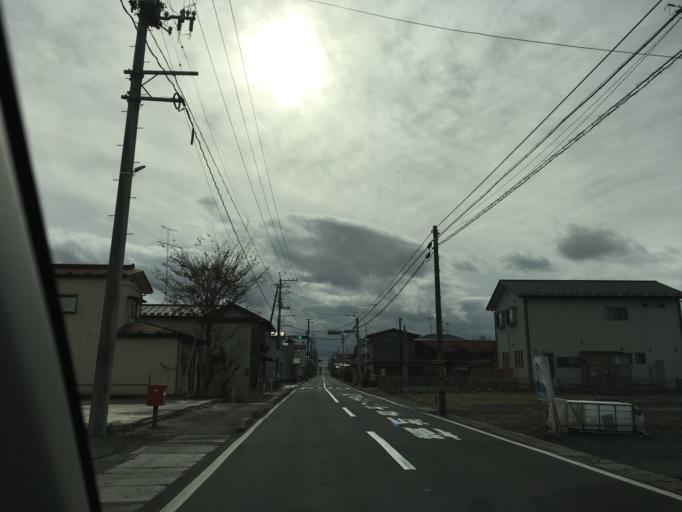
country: JP
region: Miyagi
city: Wakuya
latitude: 38.7288
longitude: 141.2718
